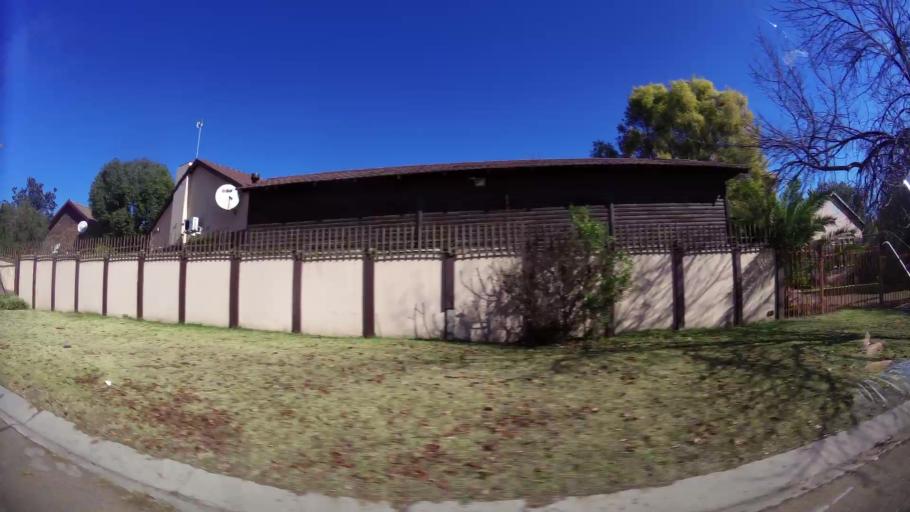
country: ZA
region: Mpumalanga
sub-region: Nkangala District Municipality
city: Witbank
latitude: -25.8748
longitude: 29.2530
